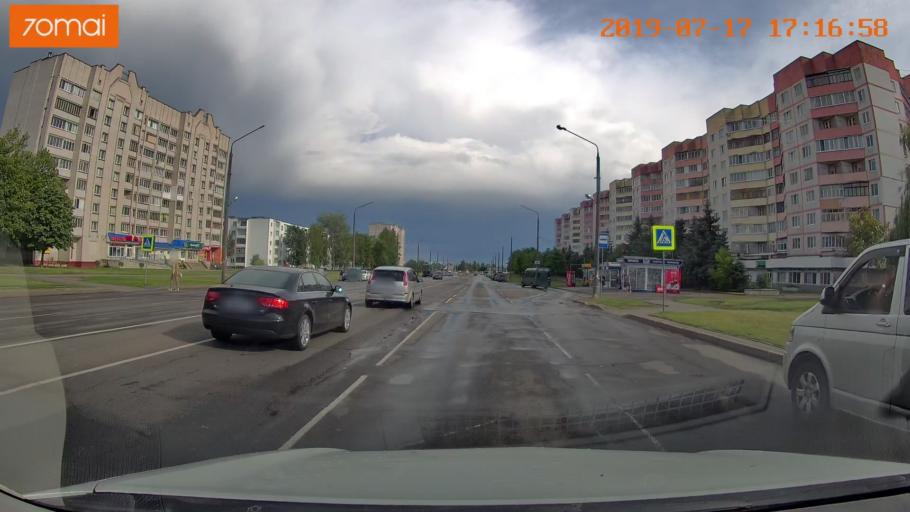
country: BY
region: Mogilev
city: Babruysk
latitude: 53.1641
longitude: 29.1964
